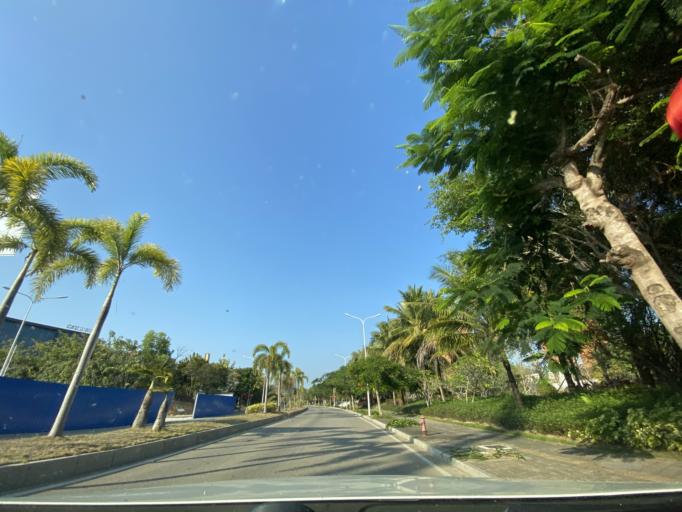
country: CN
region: Hainan
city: Haitangwan
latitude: 18.4061
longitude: 109.7808
